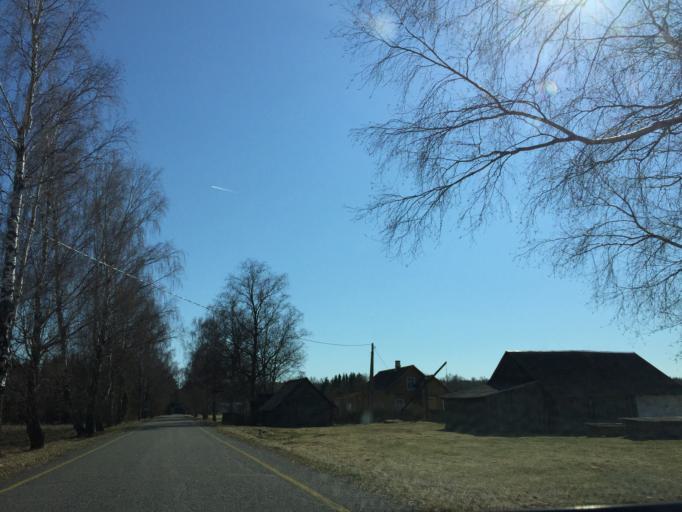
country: EE
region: Jogevamaa
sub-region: Mustvee linn
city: Mustvee
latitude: 58.9971
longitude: 27.2263
